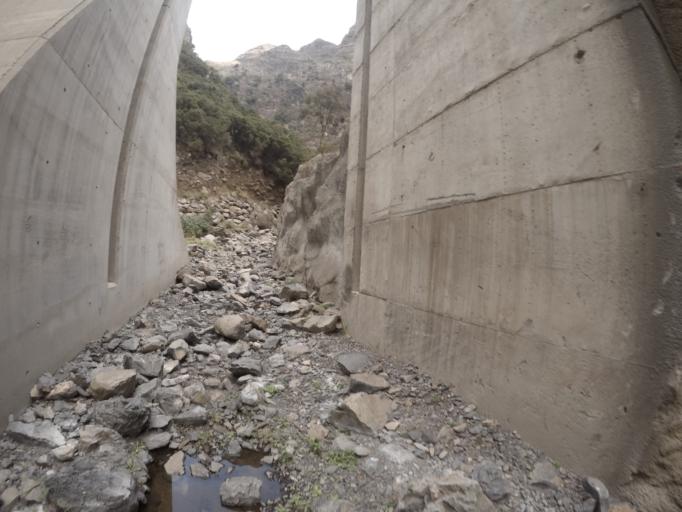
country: PT
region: Madeira
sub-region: Funchal
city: Nossa Senhora do Monte
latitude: 32.7024
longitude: -16.9203
